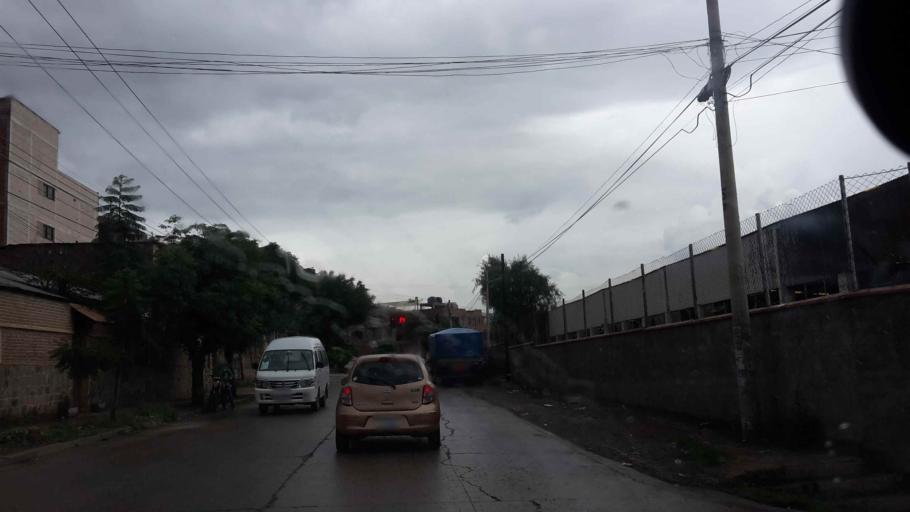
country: BO
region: Cochabamba
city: Cochabamba
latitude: -17.4200
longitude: -66.1515
